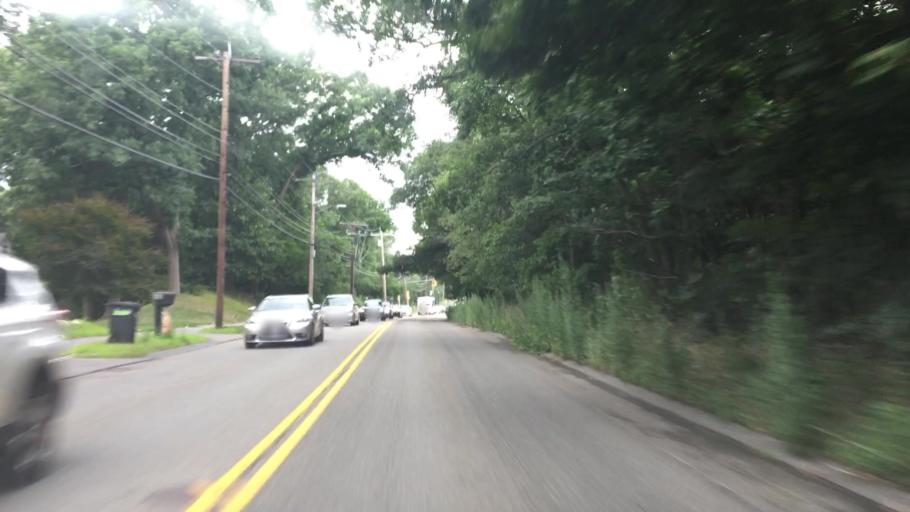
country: US
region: Massachusetts
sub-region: Middlesex County
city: Lexington
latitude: 42.4640
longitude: -71.2073
